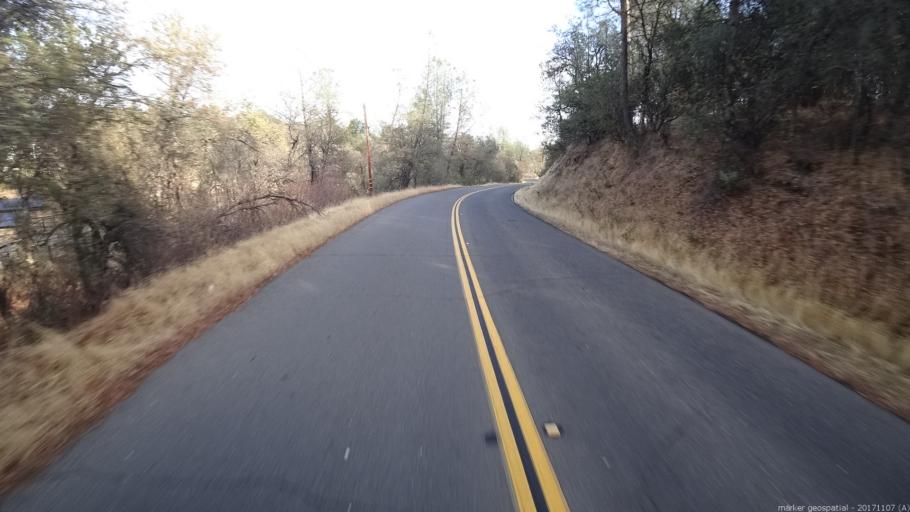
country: US
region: California
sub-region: Shasta County
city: Shasta
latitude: 40.5175
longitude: -122.4669
